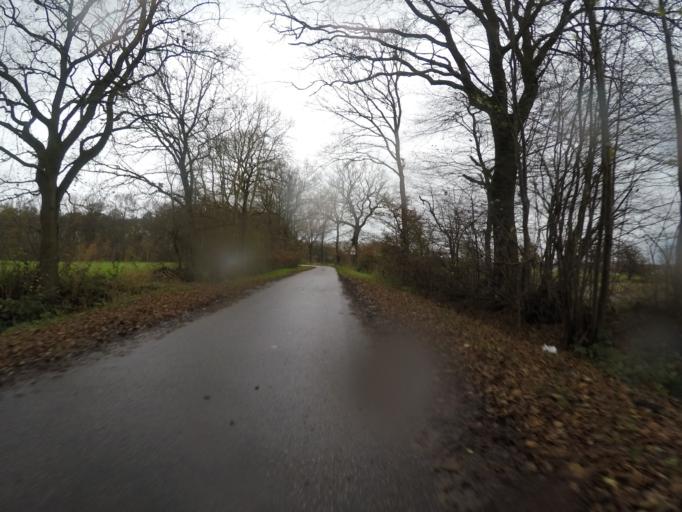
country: DE
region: Schleswig-Holstein
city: Bilsen
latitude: 53.7348
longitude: 9.8694
